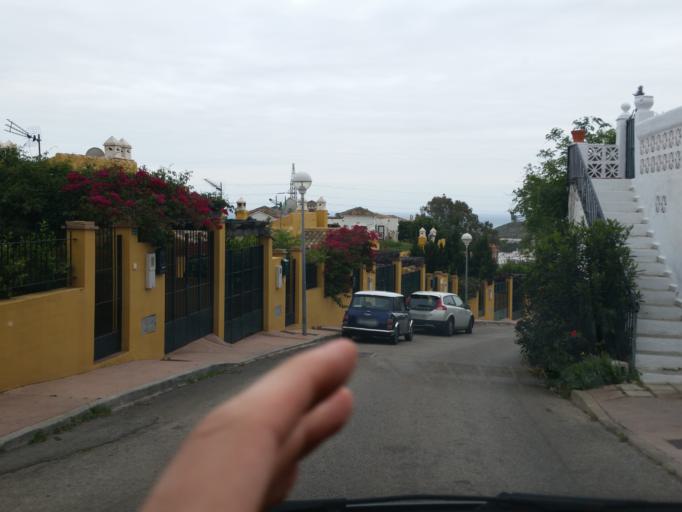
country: ES
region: Andalusia
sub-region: Provincia de Malaga
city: Fuengirola
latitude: 36.5686
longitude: -4.6094
